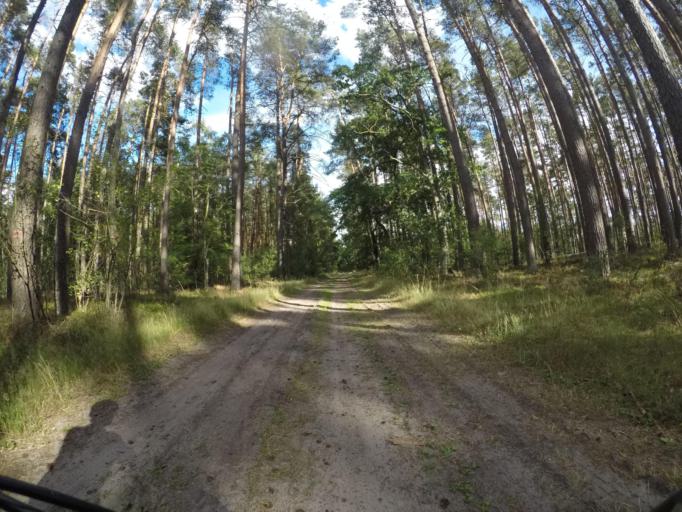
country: DE
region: Lower Saxony
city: Neu Darchau
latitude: 53.2698
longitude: 10.9810
